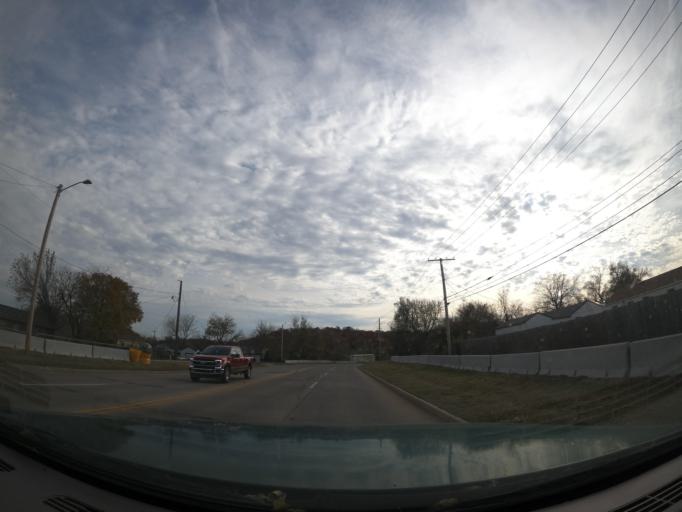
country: US
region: Oklahoma
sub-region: Tulsa County
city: Turley
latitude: 36.2188
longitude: -95.9935
